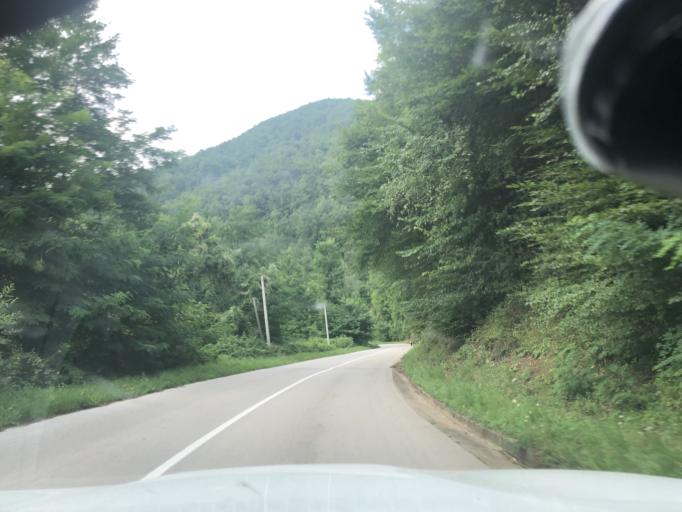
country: RS
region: Central Serbia
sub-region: Jablanicki Okrug
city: Medvega
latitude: 42.7818
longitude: 21.5910
